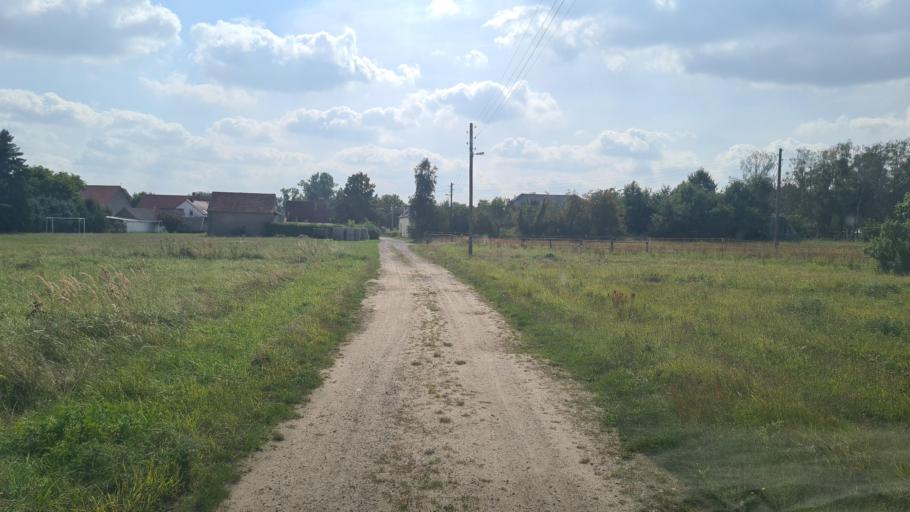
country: DE
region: Brandenburg
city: Schonewalde
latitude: 51.7370
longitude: 13.5929
